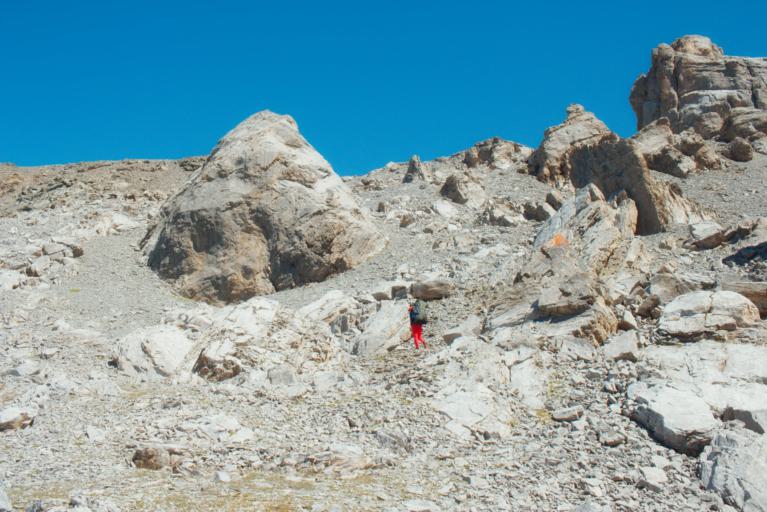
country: RU
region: Karachayevo-Cherkesiya
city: Nizhniy Arkhyz
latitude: 43.5941
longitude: 41.1831
